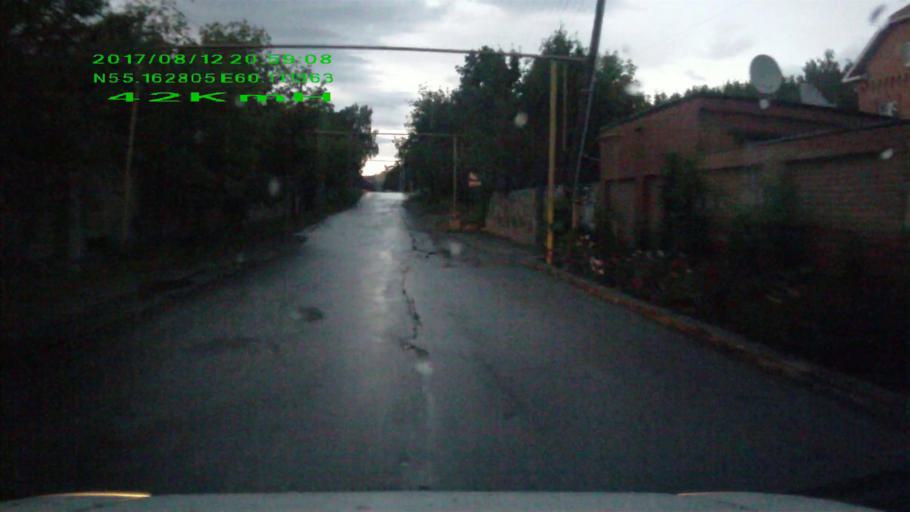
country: RU
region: Chelyabinsk
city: Turgoyak
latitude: 55.1629
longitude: 60.1114
